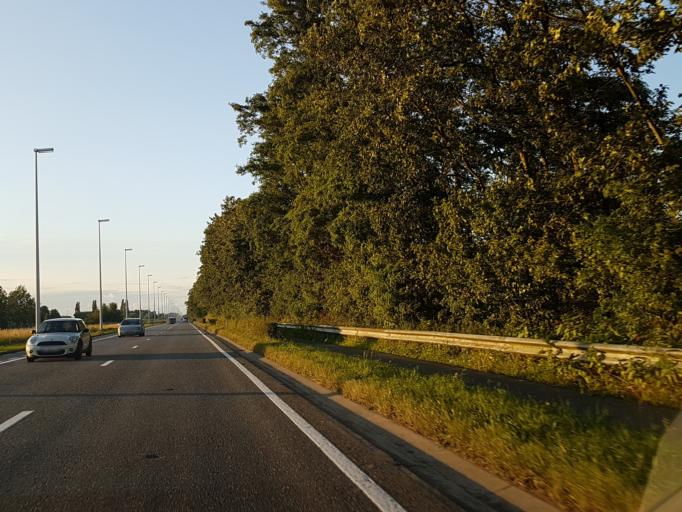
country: BE
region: Flanders
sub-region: Provincie Oost-Vlaanderen
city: Dendermonde
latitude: 51.0479
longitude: 4.1215
